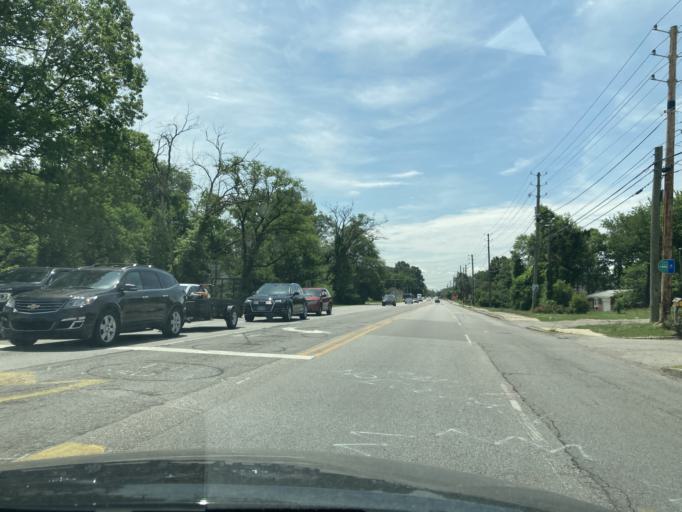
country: US
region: Indiana
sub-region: Marion County
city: Meridian Hills
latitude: 39.8679
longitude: -86.2017
